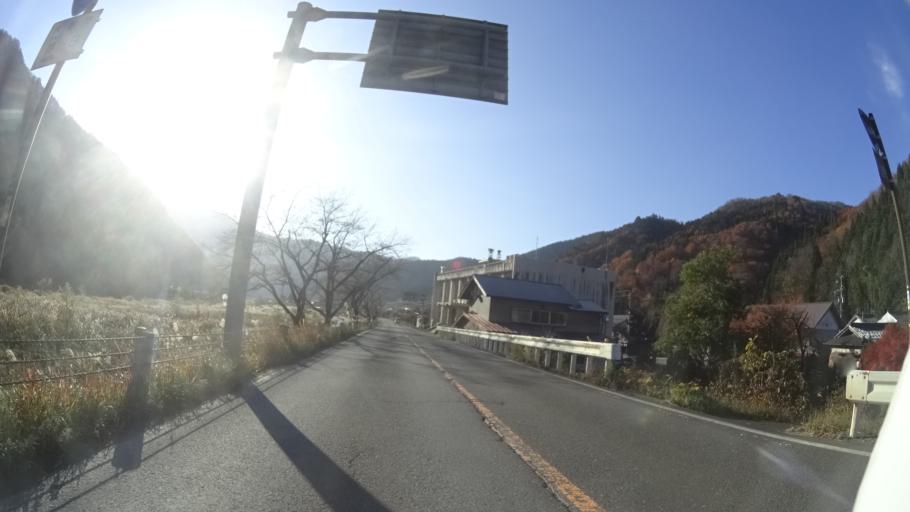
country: JP
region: Fukui
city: Ono
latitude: 35.9054
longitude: 136.6678
